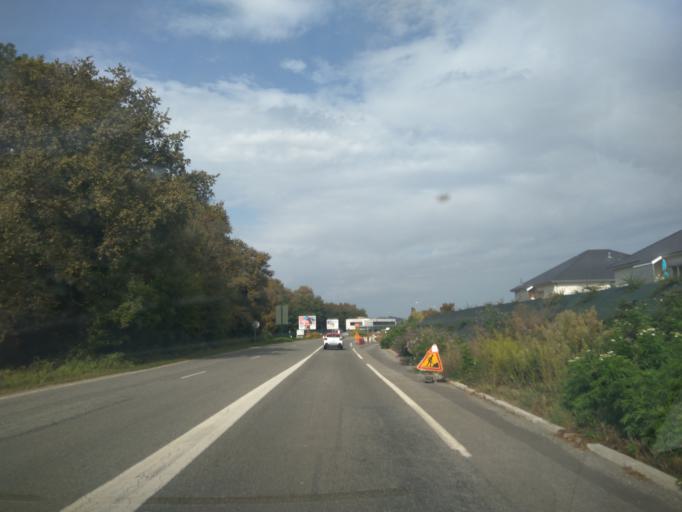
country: FR
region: Aquitaine
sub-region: Departement des Pyrenees-Atlantiques
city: Artiguelouve
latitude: 43.3164
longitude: -0.4600
